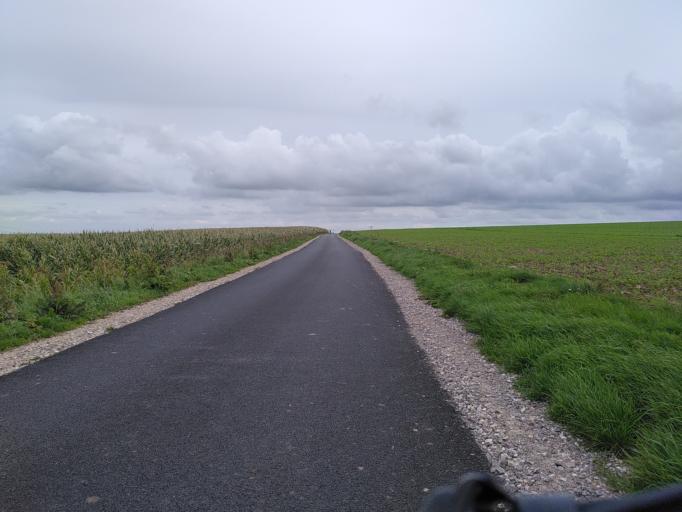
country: FR
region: Nord-Pas-de-Calais
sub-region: Departement du Pas-de-Calais
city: Desvres
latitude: 50.6481
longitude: 1.9565
